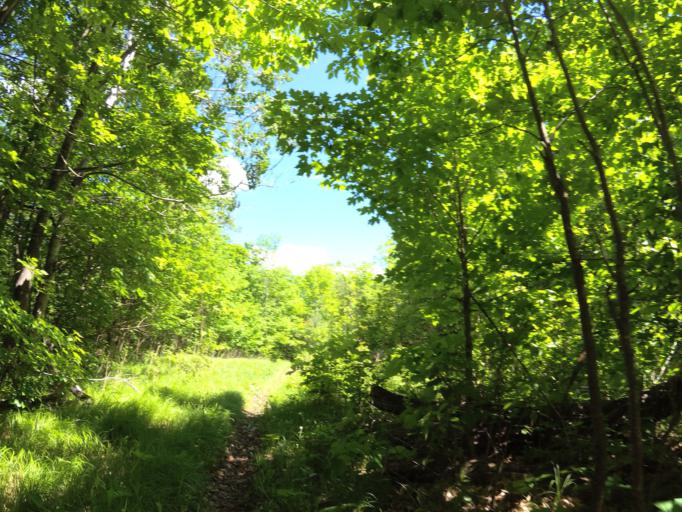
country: CA
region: Ontario
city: Renfrew
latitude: 45.0605
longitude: -76.8381
